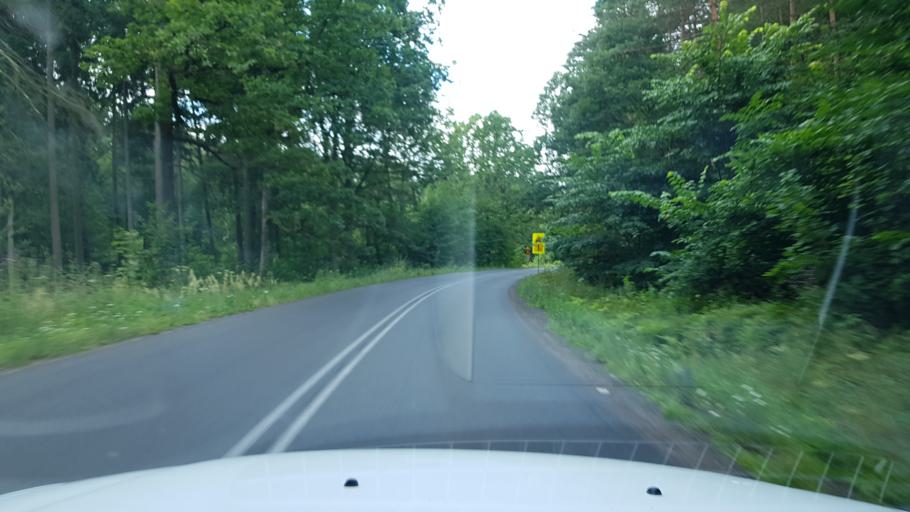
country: PL
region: West Pomeranian Voivodeship
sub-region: Powiat lobeski
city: Lobez
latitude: 53.6764
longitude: 15.6638
